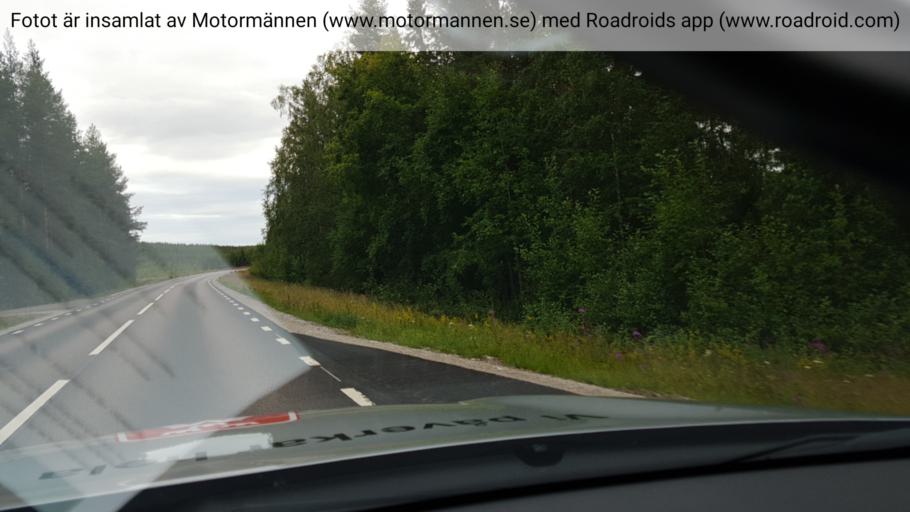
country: SE
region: Norrbotten
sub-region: Overkalix Kommun
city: OEverkalix
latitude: 66.4209
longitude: 22.8015
